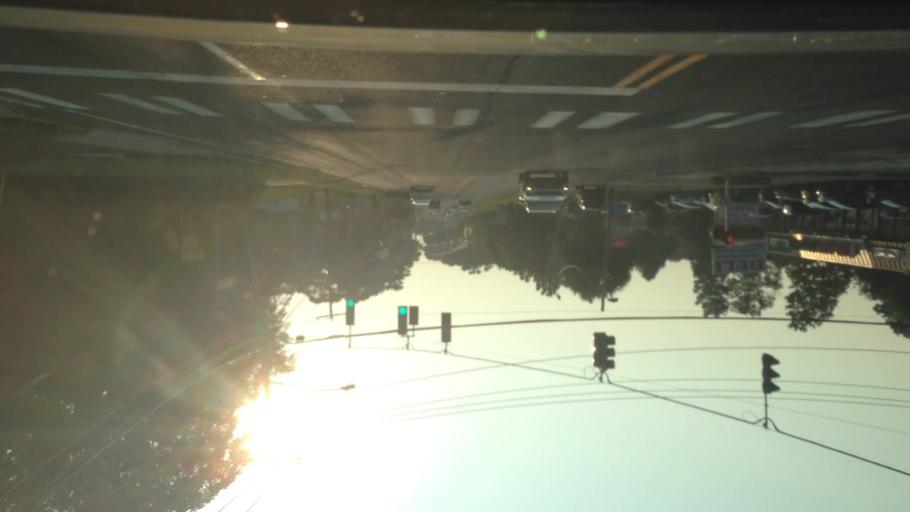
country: US
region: New York
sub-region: Suffolk County
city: Coram
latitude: 40.8690
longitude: -73.0093
